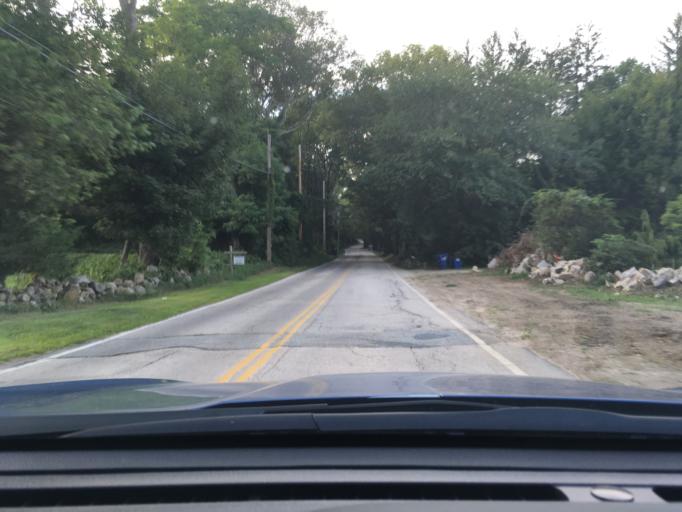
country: US
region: Rhode Island
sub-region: Washington County
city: Exeter
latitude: 41.6269
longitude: -71.5125
